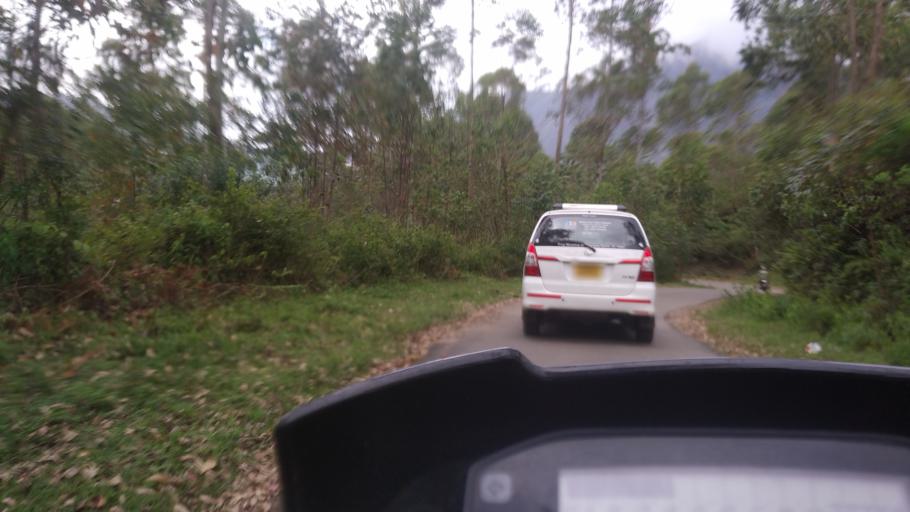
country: IN
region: Kerala
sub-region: Idukki
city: Munnar
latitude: 10.0598
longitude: 77.1077
